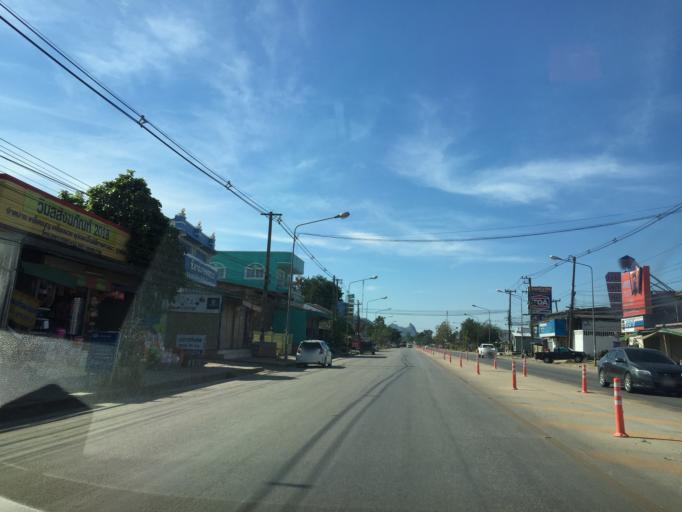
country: TH
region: Changwat Nong Bua Lamphu
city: Na Wang
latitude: 17.3233
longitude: 102.0819
